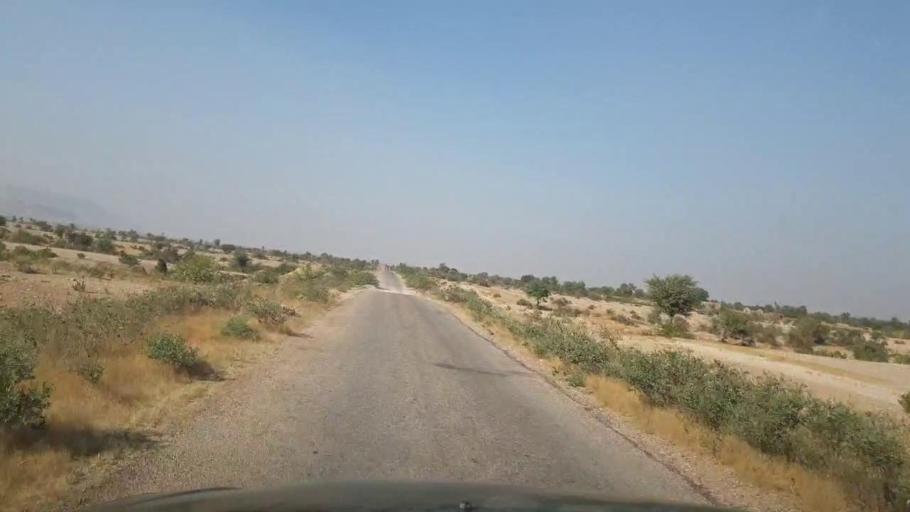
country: PK
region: Sindh
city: Jamshoro
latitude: 25.5851
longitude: 67.8203
